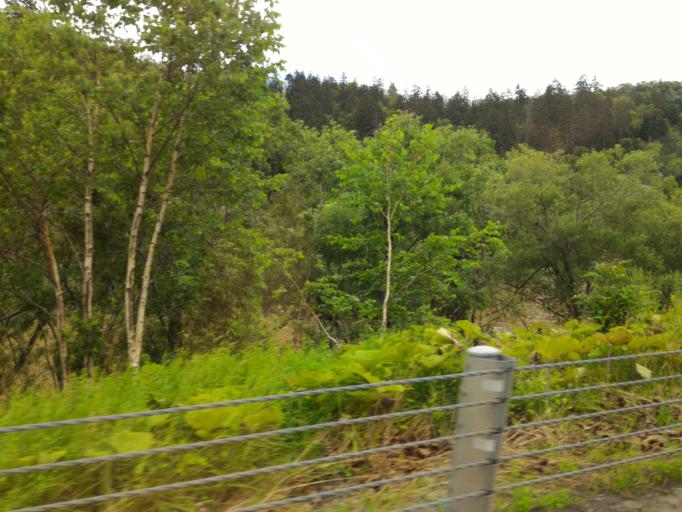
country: JP
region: Hokkaido
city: Nayoro
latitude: 44.7262
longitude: 142.2314
